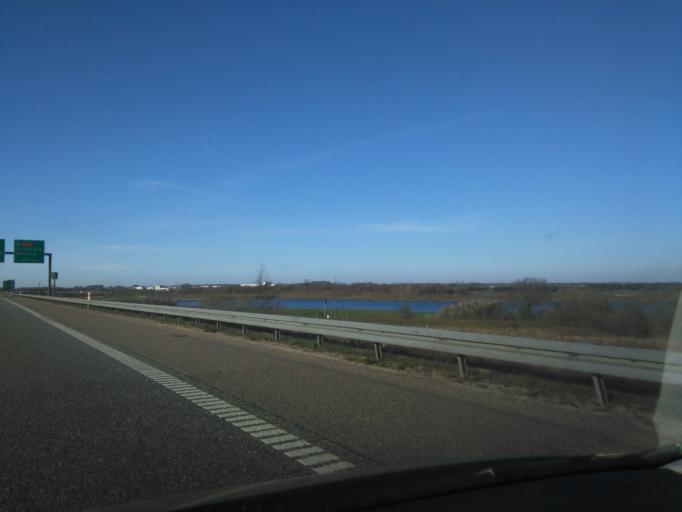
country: DK
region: Central Jutland
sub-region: Herning Kommune
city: Lind
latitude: 56.1144
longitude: 9.0108
